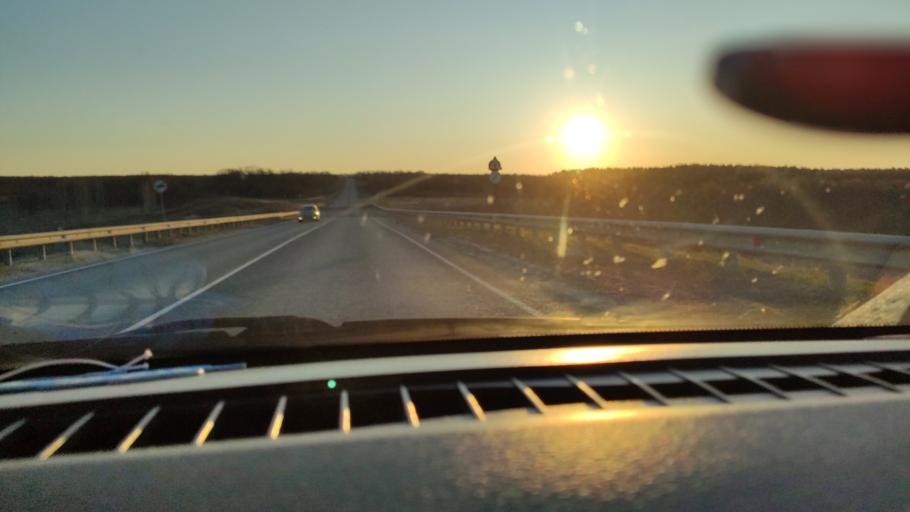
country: RU
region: Saratov
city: Sinodskoye
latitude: 51.9300
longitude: 46.5767
